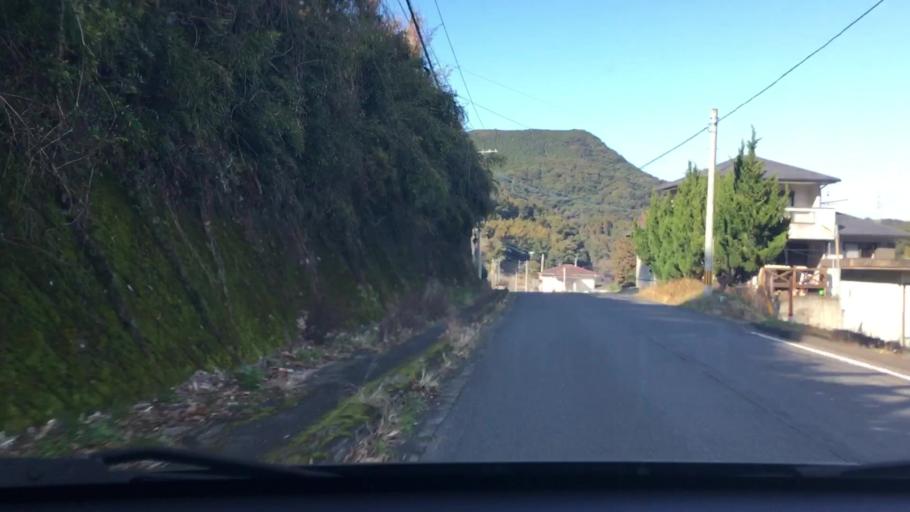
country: JP
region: Kagoshima
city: Ijuin
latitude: 31.7389
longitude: 130.4110
